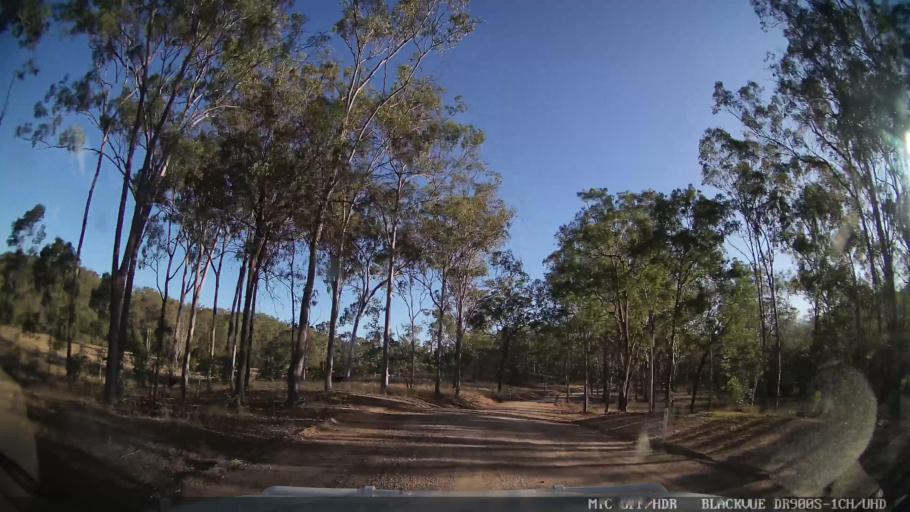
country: AU
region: Queensland
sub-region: Gladstone
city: Toolooa
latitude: -24.6944
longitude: 151.4123
